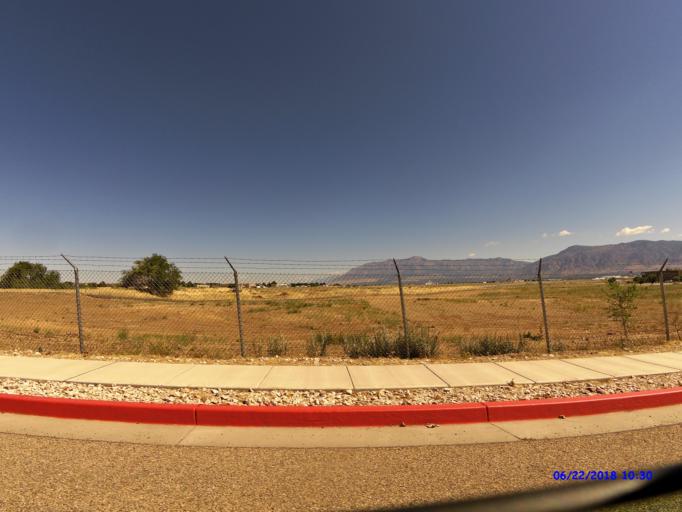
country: US
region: Utah
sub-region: Weber County
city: Riverdale
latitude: 41.1835
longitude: -112.0212
